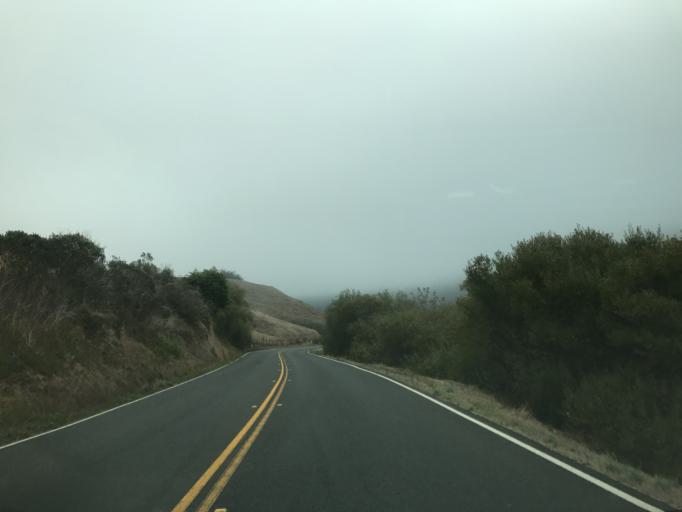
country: US
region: California
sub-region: Sonoma County
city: Monte Rio
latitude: 38.4459
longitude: -123.0830
